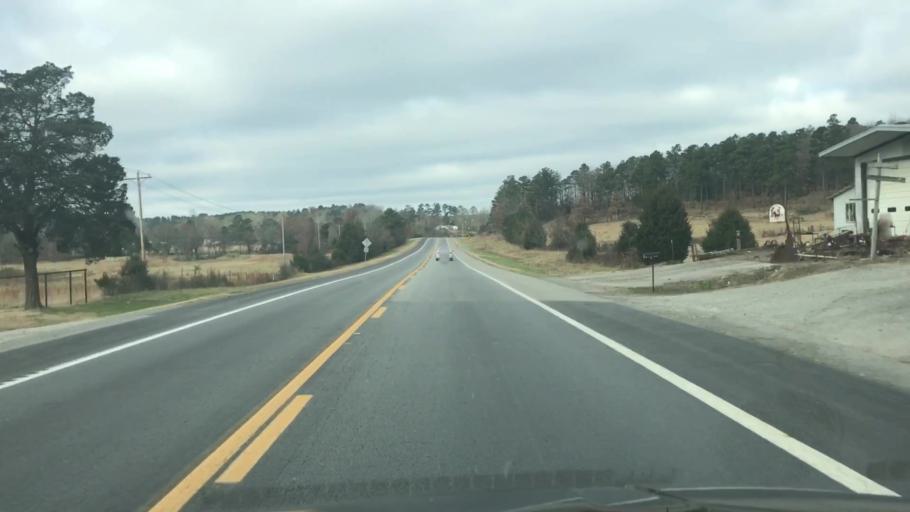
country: US
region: Arkansas
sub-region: Scott County
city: Waldron
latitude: 34.8380
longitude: -94.0477
